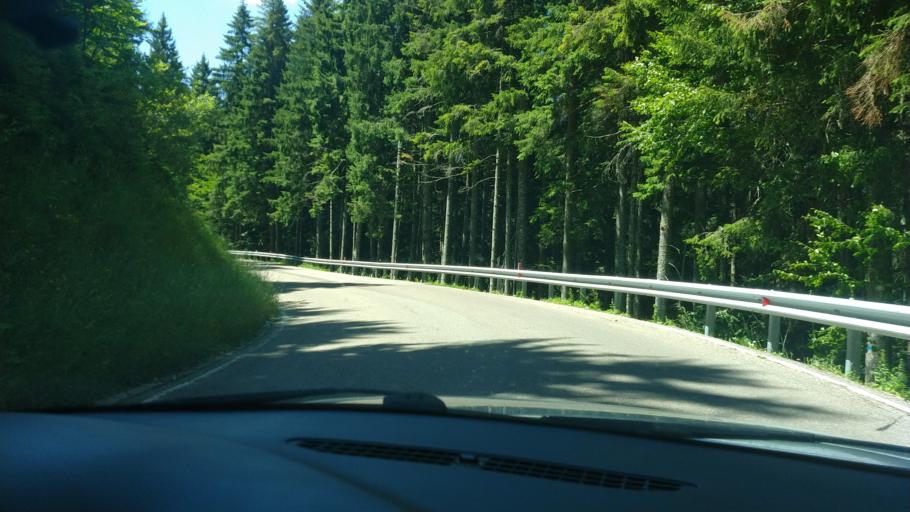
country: IT
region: Veneto
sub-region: Provincia di Vicenza
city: Lastebasse
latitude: 45.9097
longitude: 11.2257
